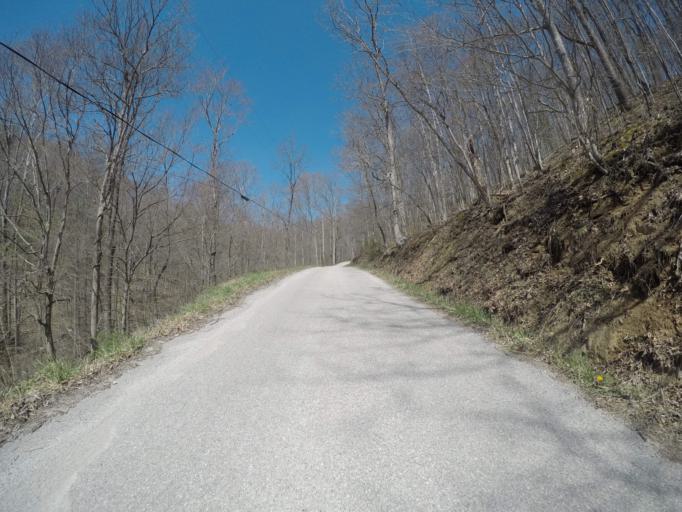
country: US
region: West Virginia
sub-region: Kanawha County
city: Charleston
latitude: 38.4117
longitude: -81.5876
